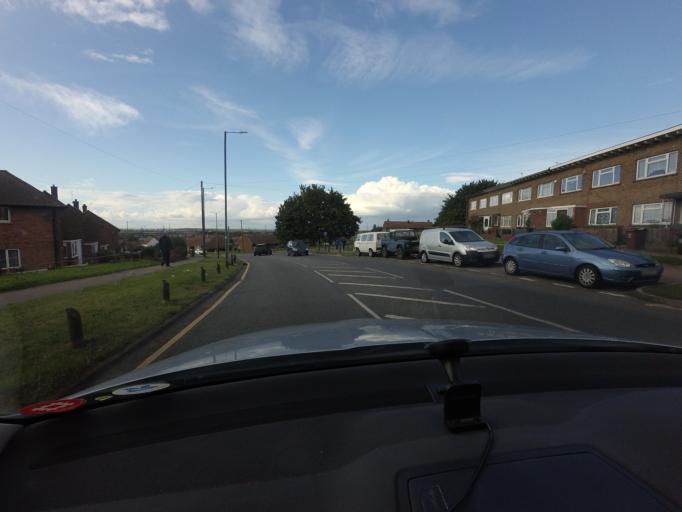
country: GB
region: England
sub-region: Kent
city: Dartford
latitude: 51.4520
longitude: 0.2269
